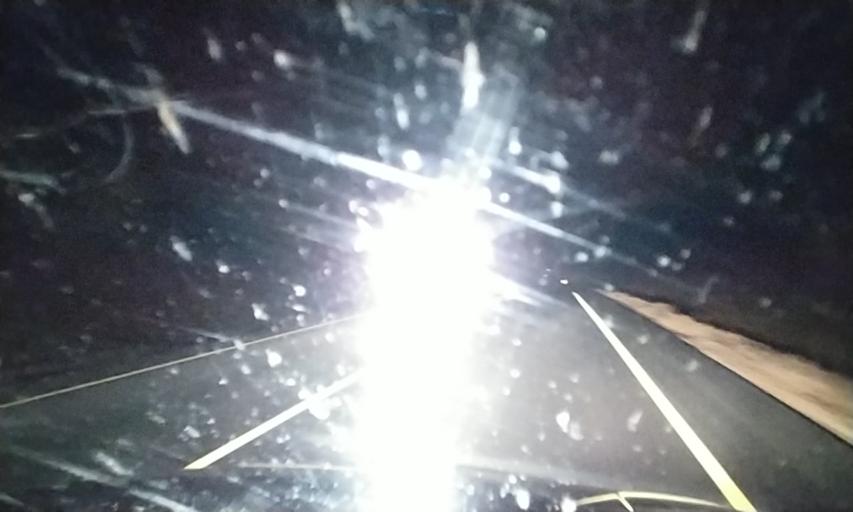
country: ES
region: Castille and Leon
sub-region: Provincia de Salamanca
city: Robleda
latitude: 40.3618
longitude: -6.6232
